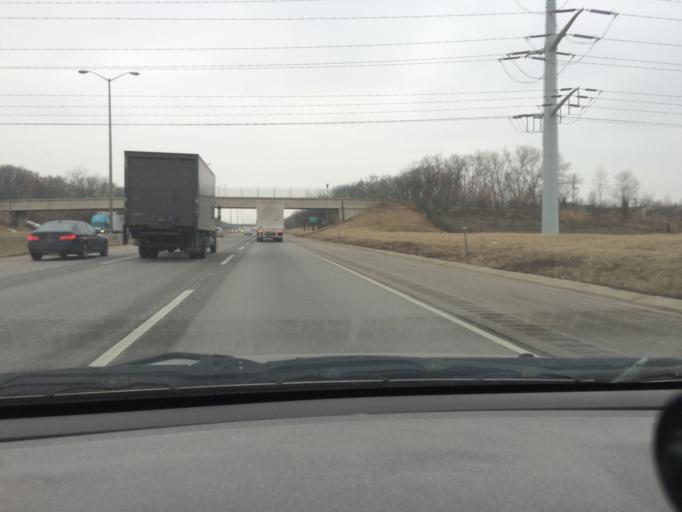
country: US
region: Illinois
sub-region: DuPage County
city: Lombard
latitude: 41.8917
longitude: -88.0375
